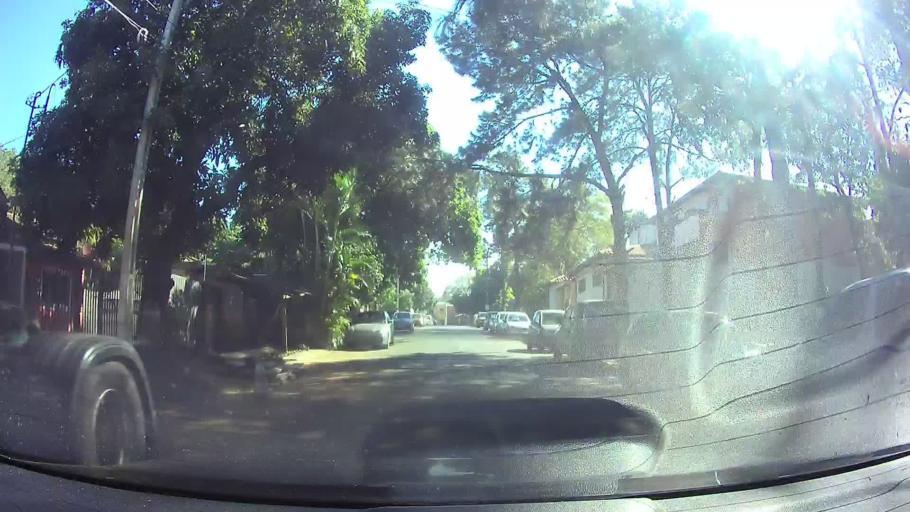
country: PY
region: Central
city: Villa Elisa
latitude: -25.3765
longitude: -57.5818
